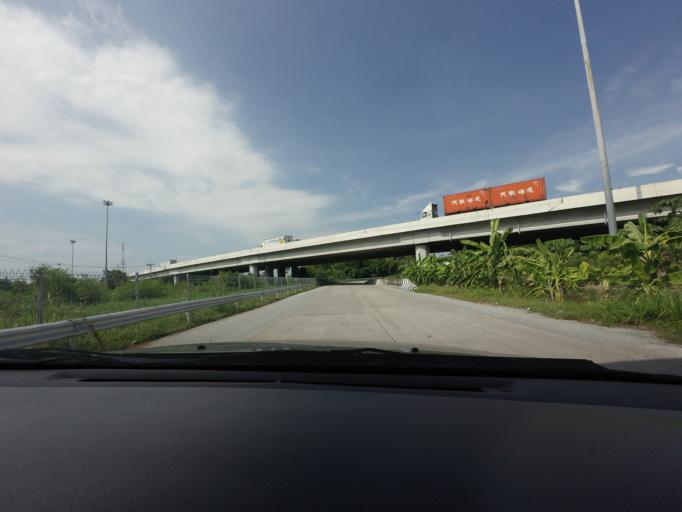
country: TH
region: Chon Buri
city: Chon Buri
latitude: 13.3317
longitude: 100.9887
